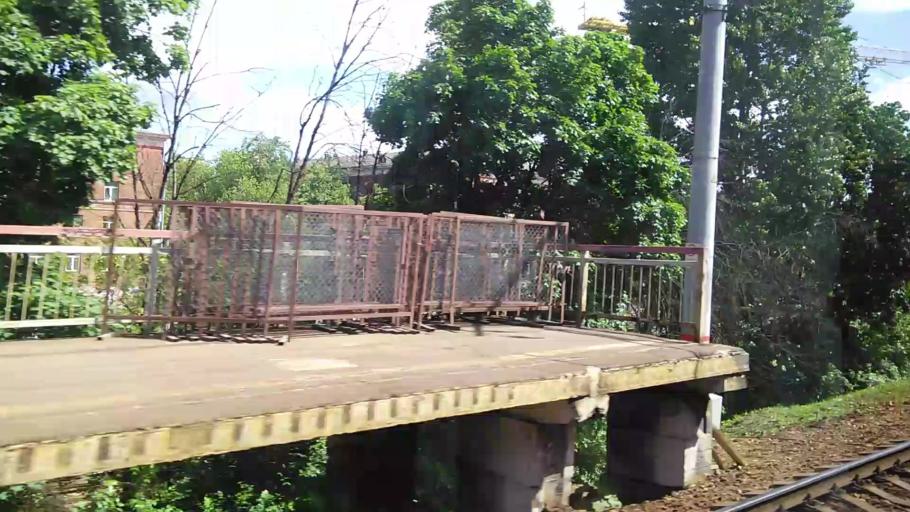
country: RU
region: Moscow
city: Likhobory
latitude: 55.8456
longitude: 37.5748
